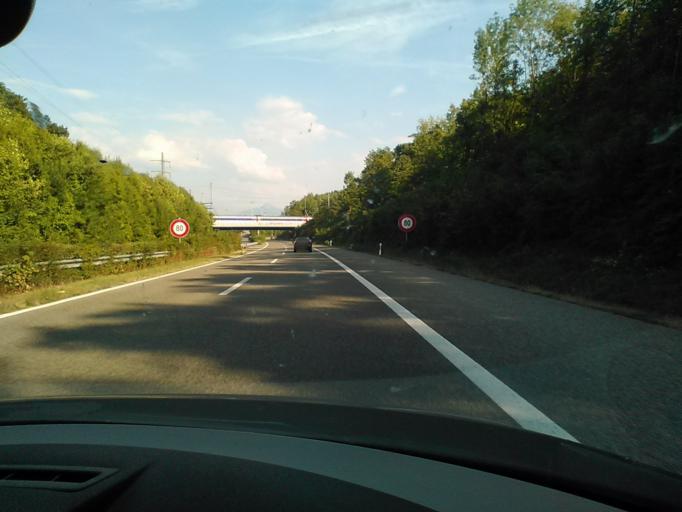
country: CH
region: Geneva
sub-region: Geneva
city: Bellevue
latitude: 46.2494
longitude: 6.1445
